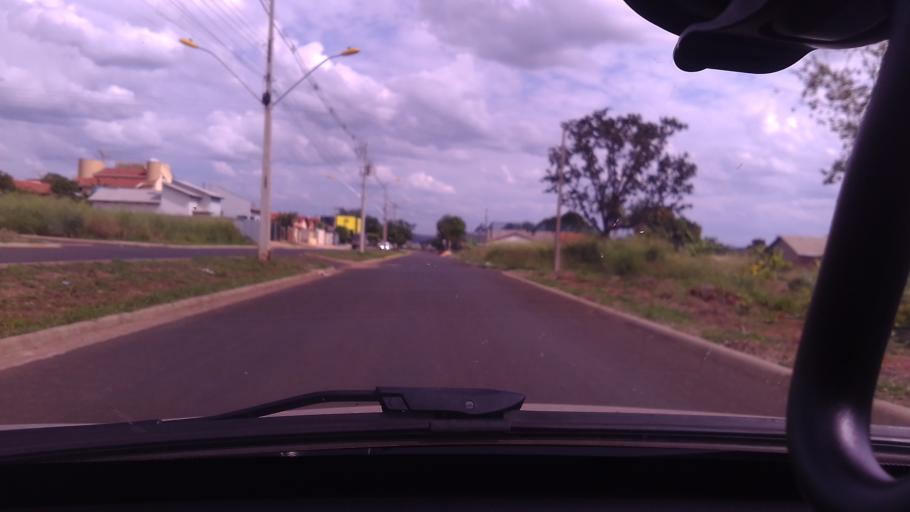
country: BR
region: Goias
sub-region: Mineiros
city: Mineiros
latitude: -17.5777
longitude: -52.5549
